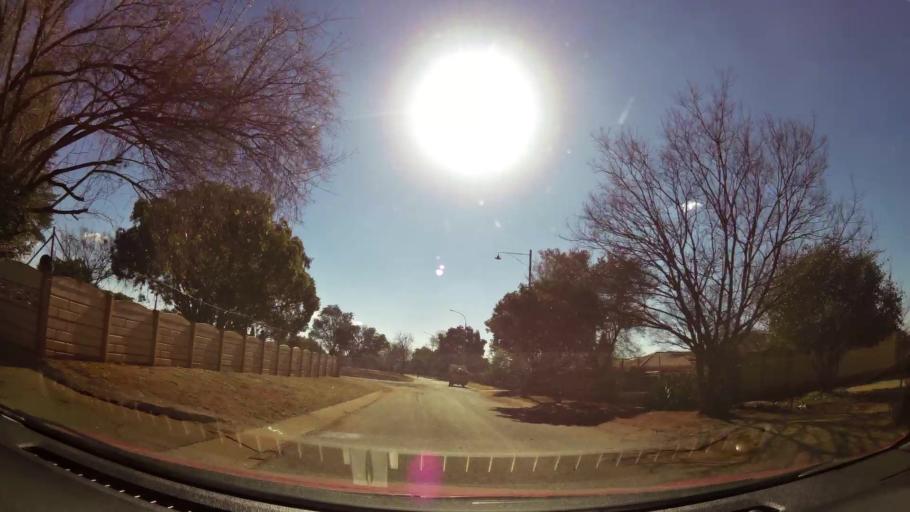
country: ZA
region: Gauteng
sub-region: West Rand District Municipality
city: Carletonville
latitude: -26.3678
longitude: 27.3805
